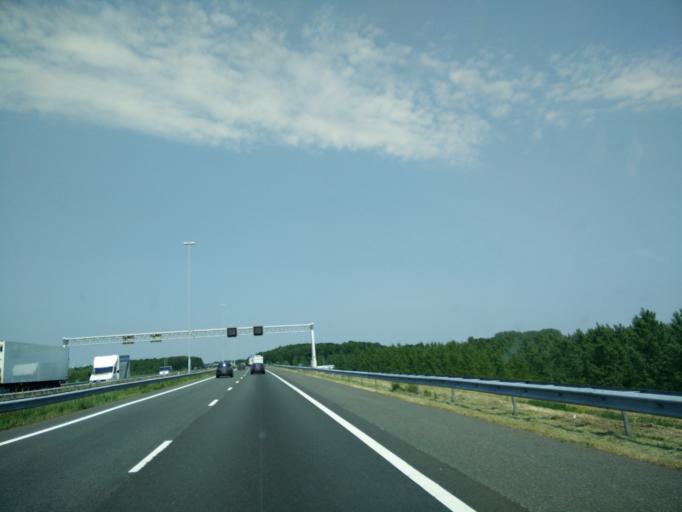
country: NL
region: Utrecht
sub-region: Gemeente Vianen
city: Vianen
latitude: 51.9733
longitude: 5.0999
